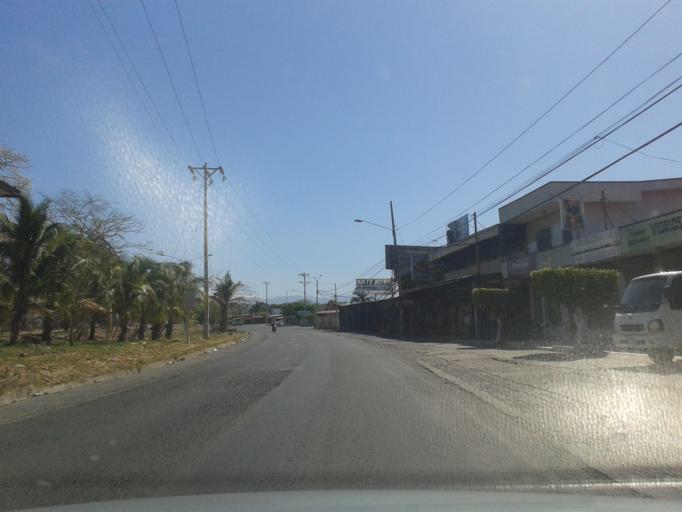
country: CR
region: Puntarenas
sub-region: Canton Central de Puntarenas
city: Chacarita
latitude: 9.9780
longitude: -84.7270
